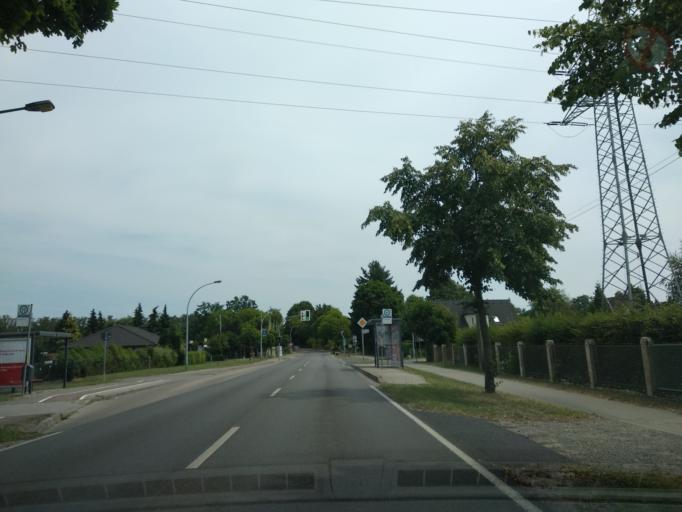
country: DE
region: Brandenburg
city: Oranienburg
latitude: 52.7518
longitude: 13.2179
